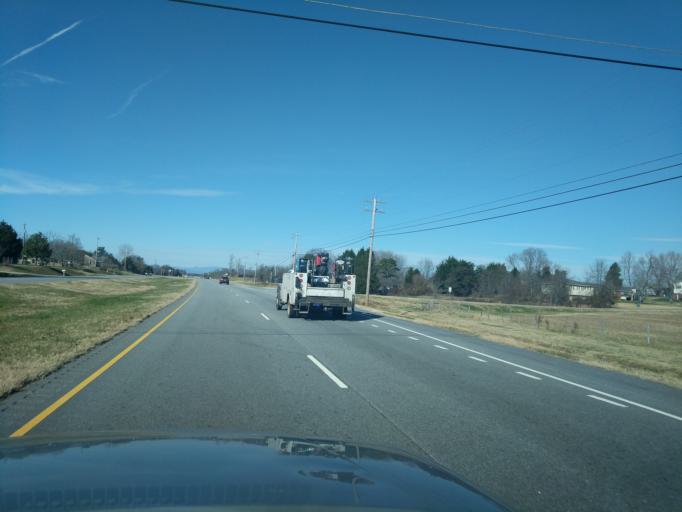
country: US
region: North Carolina
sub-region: Rutherford County
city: Forest City
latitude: 35.2799
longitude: -81.8973
